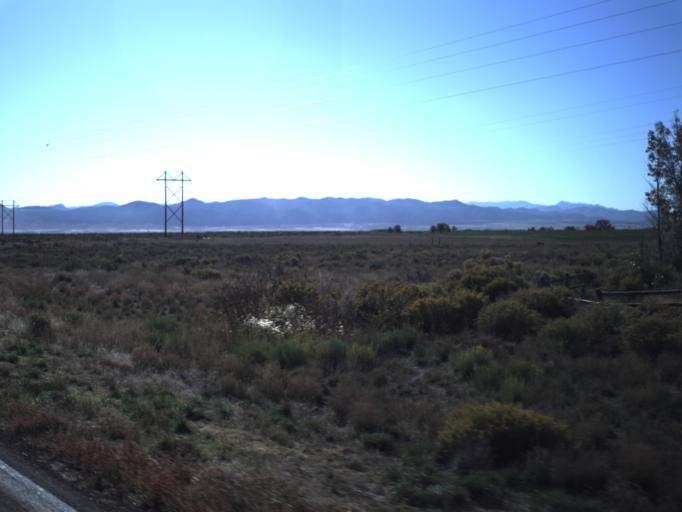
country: US
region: Utah
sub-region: Washington County
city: Enterprise
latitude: 37.7073
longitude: -113.6501
